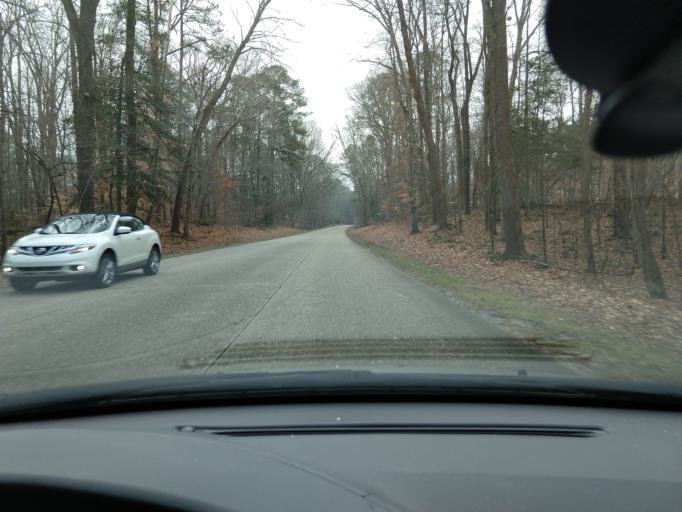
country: US
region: Virginia
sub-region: City of Williamsburg
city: Williamsburg
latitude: 37.2789
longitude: -76.6203
